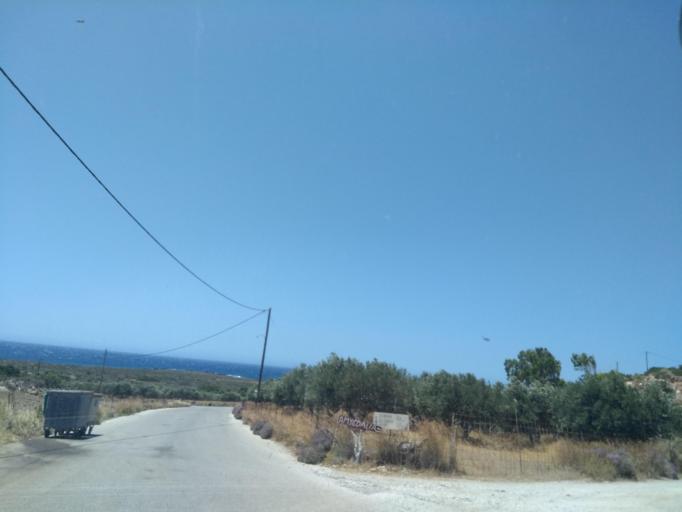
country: GR
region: Crete
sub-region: Nomos Chanias
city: Vryses
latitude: 35.3400
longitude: 23.5444
